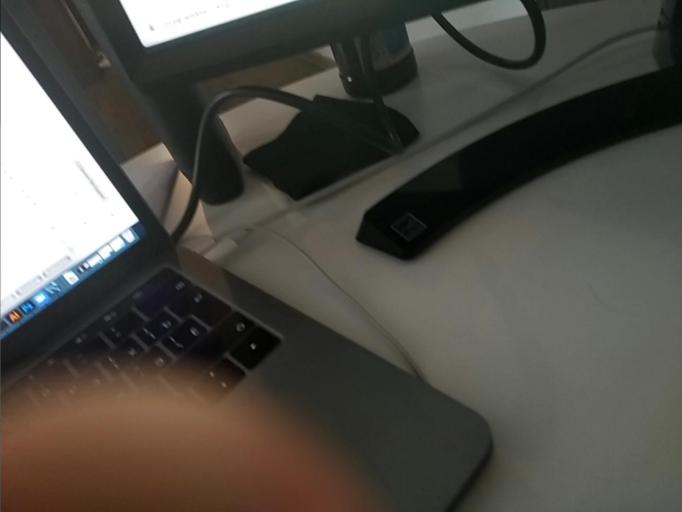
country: RU
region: Moskovskaya
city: Balashikha
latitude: 55.8084
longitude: 37.9584
